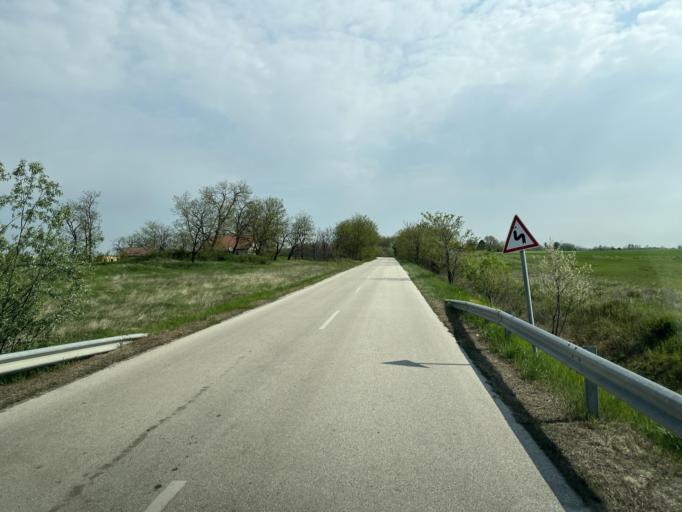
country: HU
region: Pest
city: Jaszkarajeno
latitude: 47.0807
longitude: 20.0117
